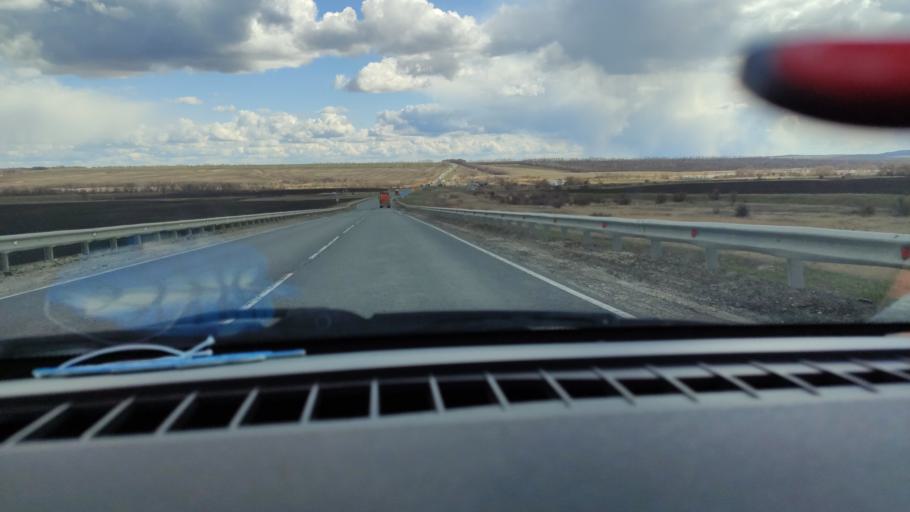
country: RU
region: Saratov
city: Dukhovnitskoye
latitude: 52.7459
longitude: 48.2517
